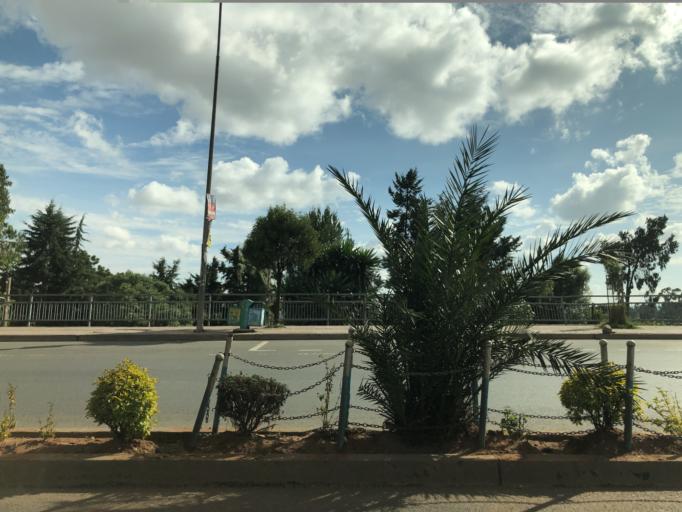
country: ET
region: Adis Abeba
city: Addis Ababa
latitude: 9.0315
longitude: 38.7709
